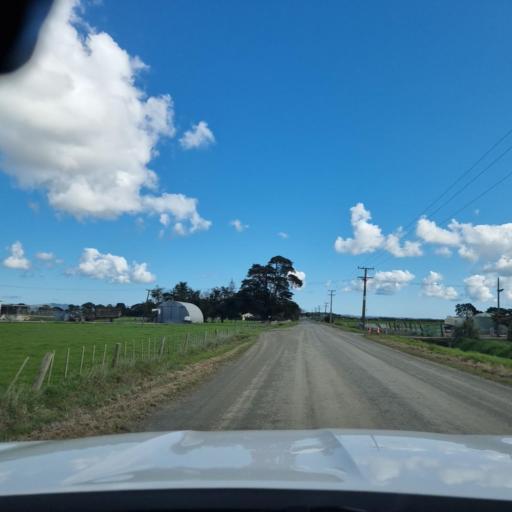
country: NZ
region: Northland
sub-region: Kaipara District
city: Dargaville
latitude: -36.1515
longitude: 174.0762
